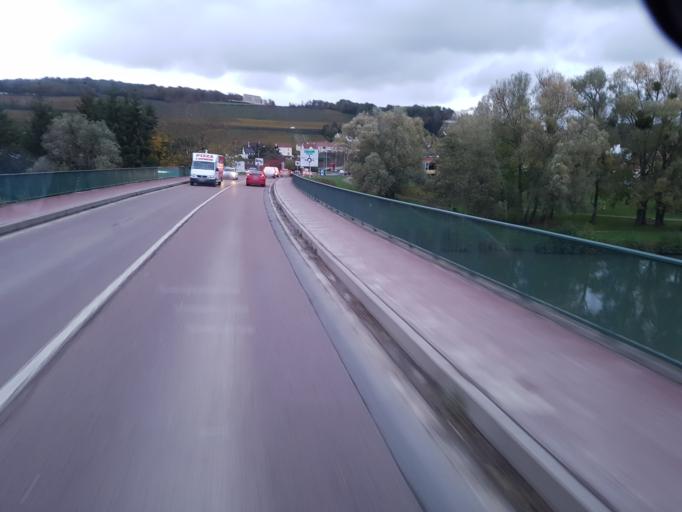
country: FR
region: Picardie
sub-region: Departement de l'Aisne
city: Essomes-sur-Marne
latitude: 49.0346
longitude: 3.3831
